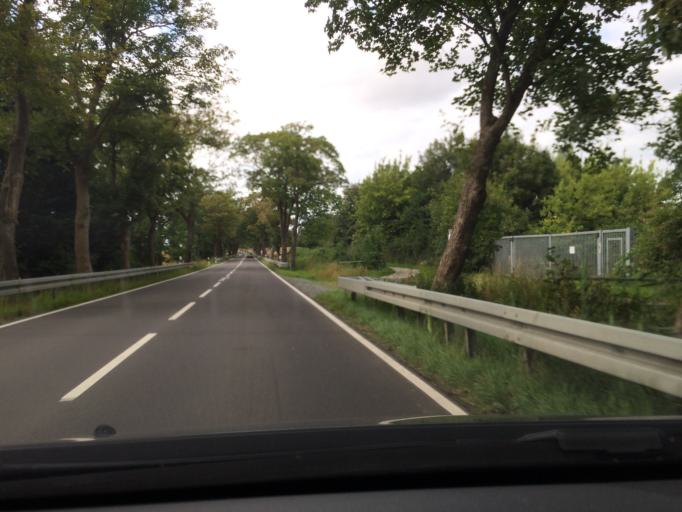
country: DE
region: Mecklenburg-Vorpommern
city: Kramerhof
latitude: 54.3450
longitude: 13.0486
